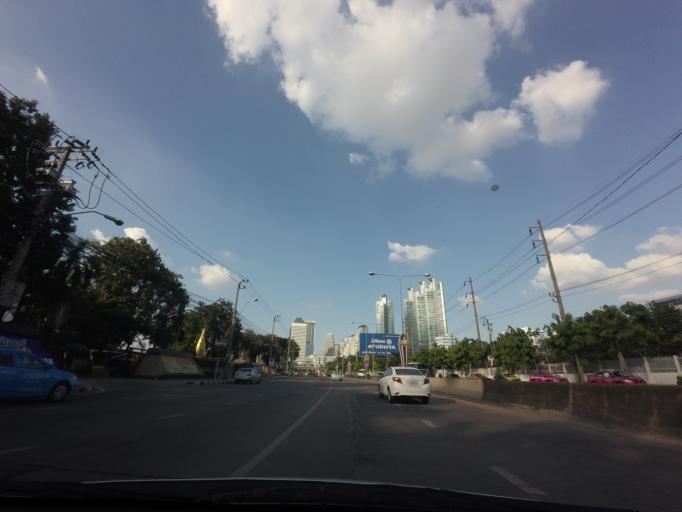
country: TH
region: Bangkok
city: Khlong Toei
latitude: 13.7239
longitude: 100.5602
